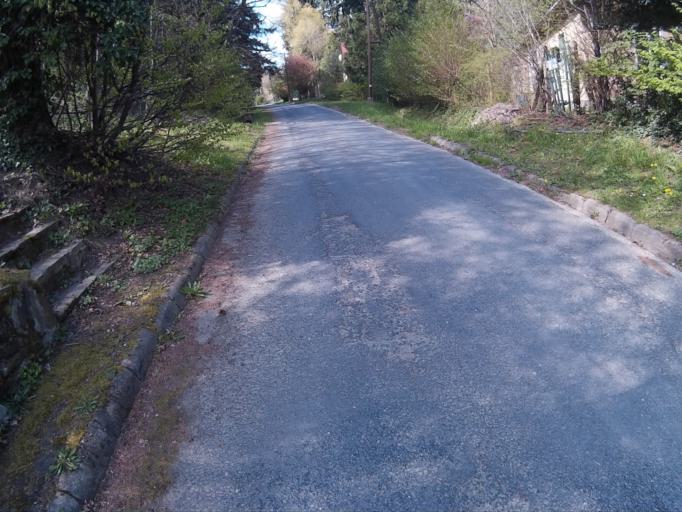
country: AT
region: Burgenland
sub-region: Politischer Bezirk Oberwart
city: Rechnitz
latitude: 47.3462
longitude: 16.4888
